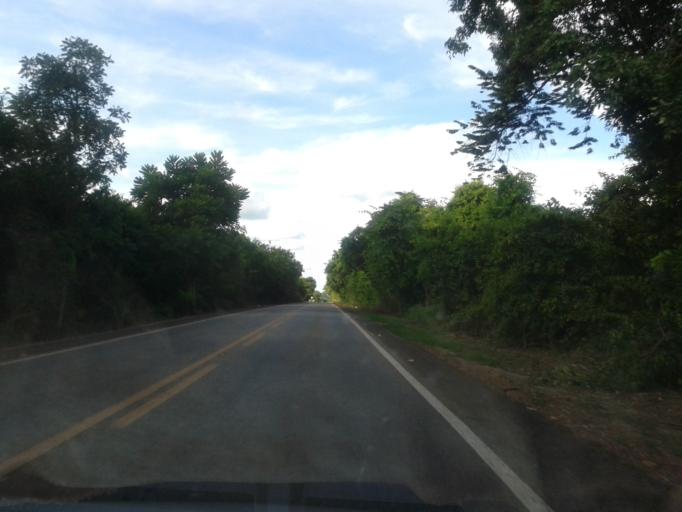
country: BR
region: Goias
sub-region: Mozarlandia
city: Mozarlandia
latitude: -14.5968
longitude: -50.5102
